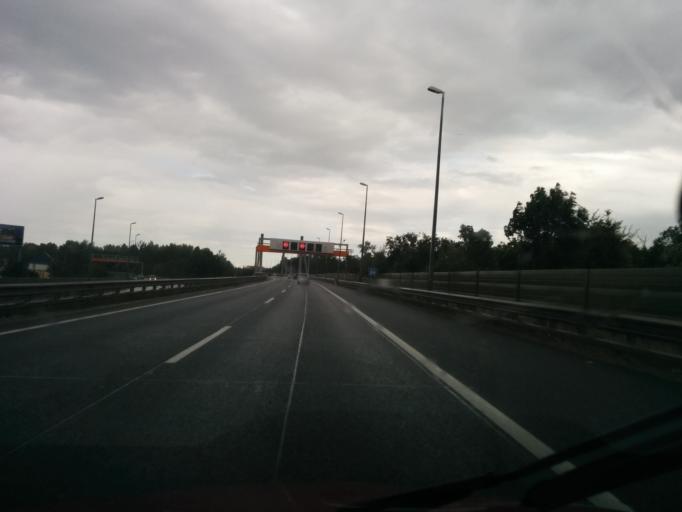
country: AT
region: Lower Austria
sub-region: Politischer Bezirk Wien-Umgebung
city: Schwechat
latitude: 48.1784
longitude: 16.4532
